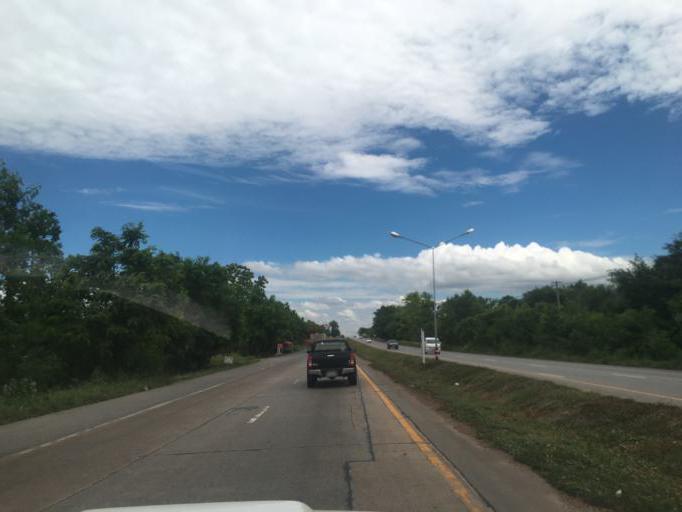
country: TH
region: Khon Kaen
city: Nam Phong
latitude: 16.6495
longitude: 102.8002
